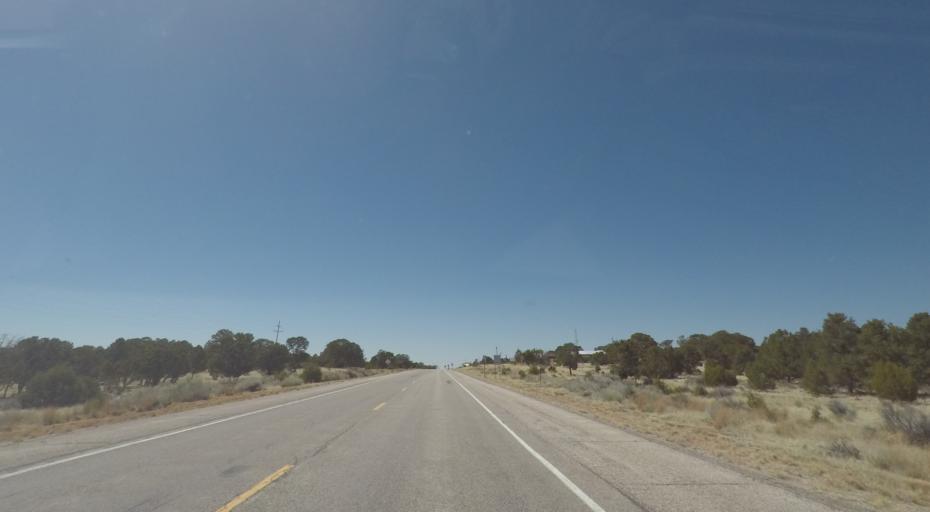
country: US
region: New Mexico
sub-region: Socorro County
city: Alamo
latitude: 34.2969
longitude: -108.1234
